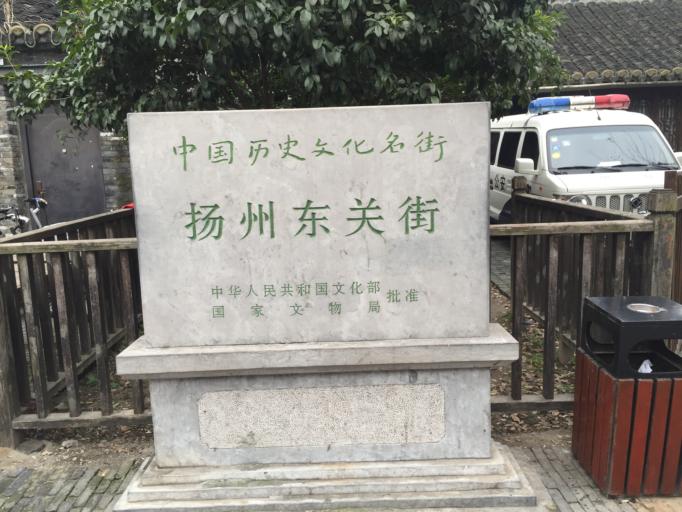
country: CN
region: Jiangsu Sheng
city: Yangzhou
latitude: 32.3998
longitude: 119.4451
